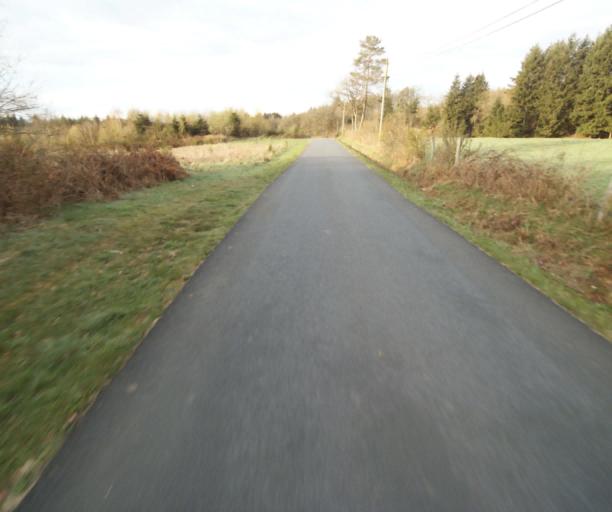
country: FR
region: Limousin
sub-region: Departement de la Correze
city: Correze
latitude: 45.4077
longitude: 1.8746
